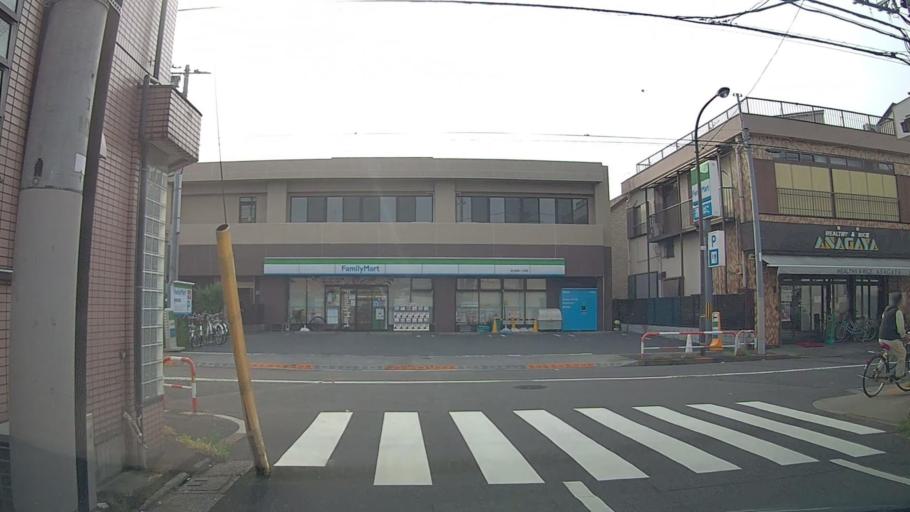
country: JP
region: Saitama
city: Kawaguchi
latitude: 35.7594
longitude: 139.7581
